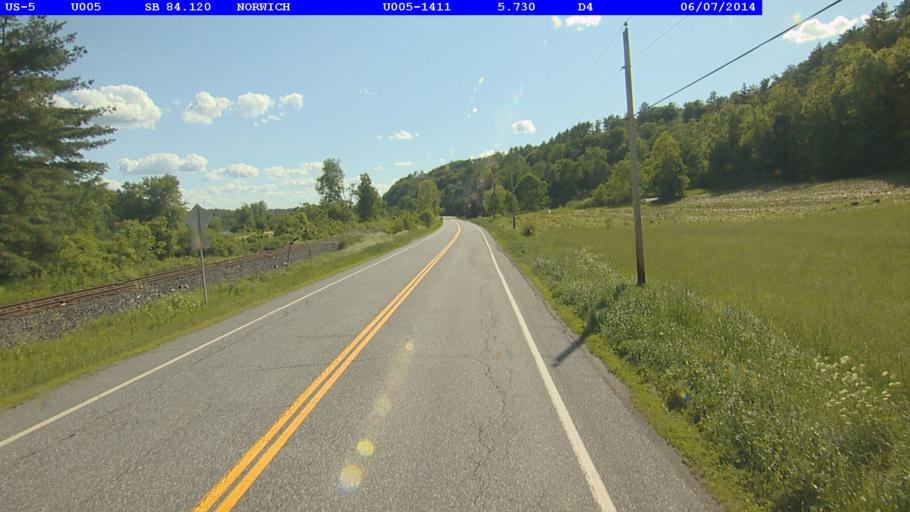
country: US
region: New Hampshire
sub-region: Grafton County
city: Hanover
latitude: 43.7460
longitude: -72.2400
